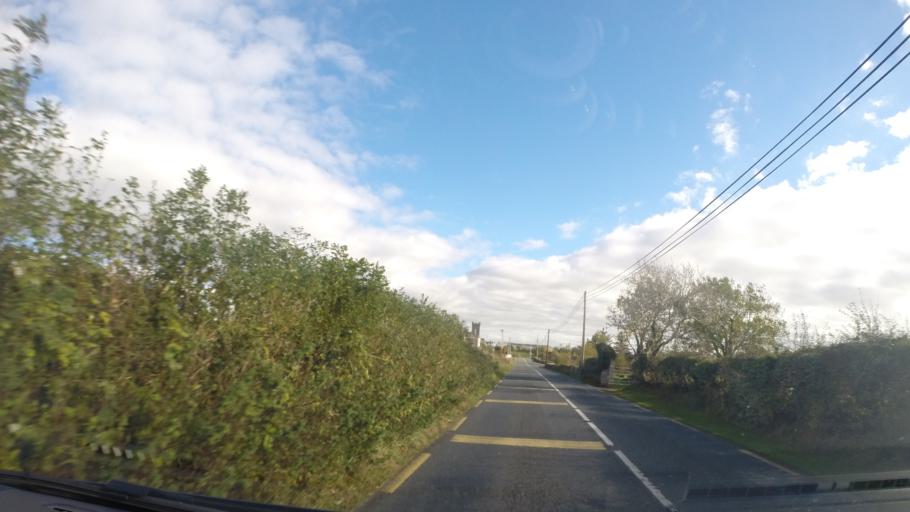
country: IE
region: Ulster
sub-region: County Donegal
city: Killybegs
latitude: 54.6316
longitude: -8.3745
